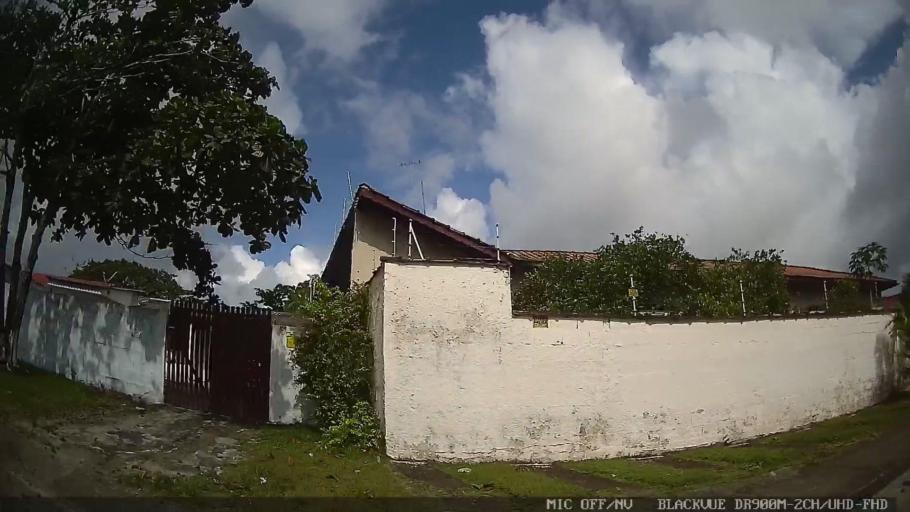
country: BR
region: Sao Paulo
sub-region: Itanhaem
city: Itanhaem
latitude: -24.2365
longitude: -46.8841
